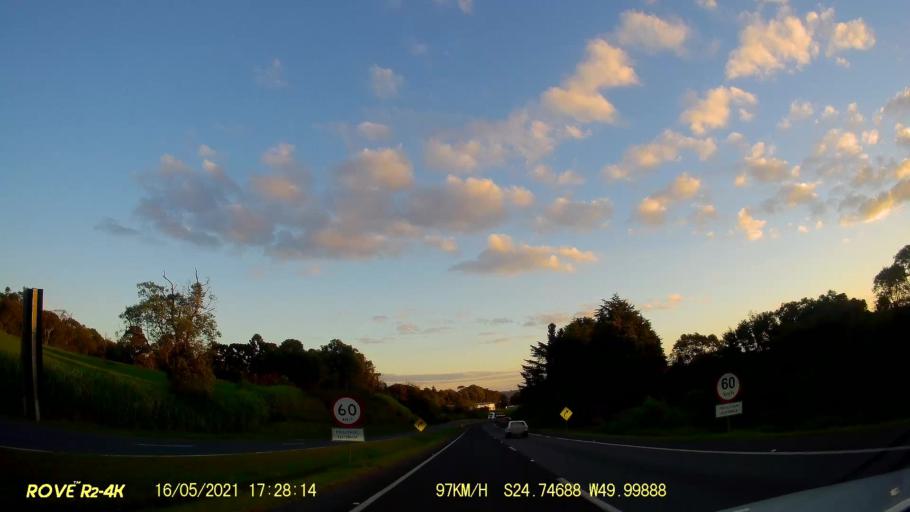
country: BR
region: Parana
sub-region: Castro
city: Castro
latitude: -24.7470
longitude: -49.9994
